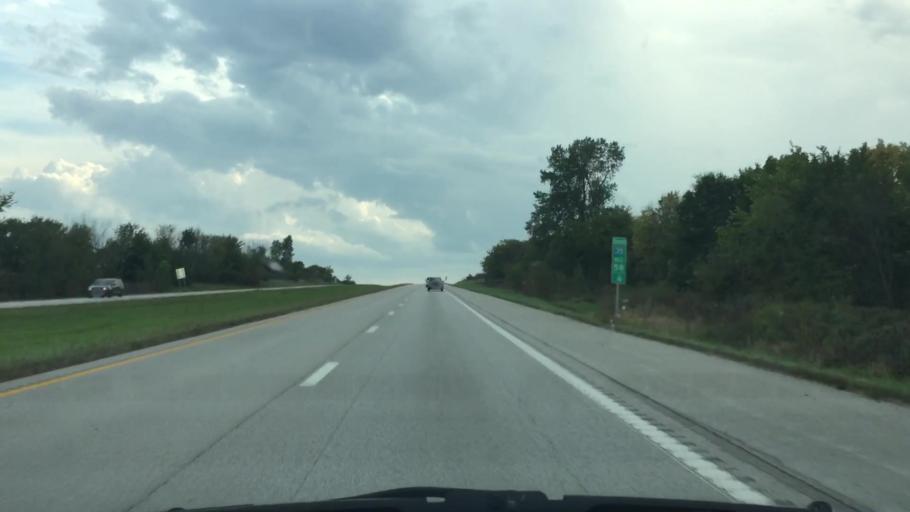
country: US
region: Missouri
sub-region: Clinton County
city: Cameron
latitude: 39.8141
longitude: -94.1944
